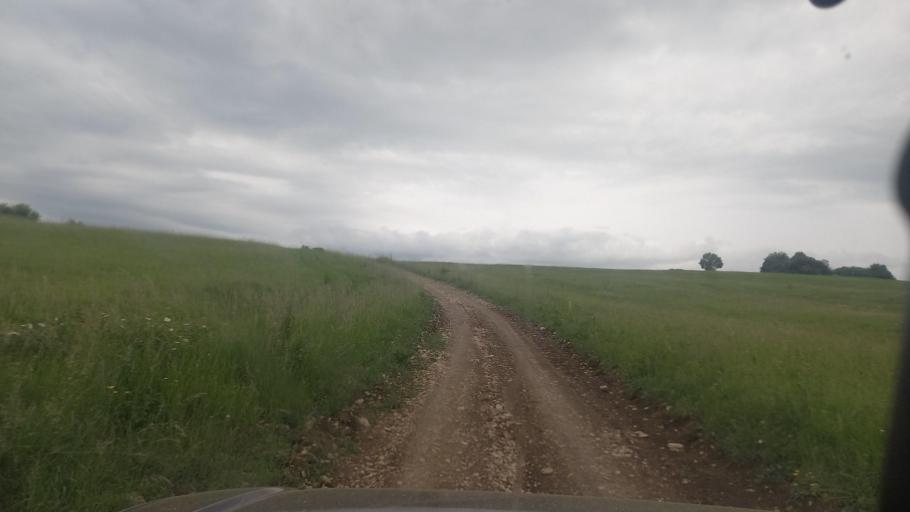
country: RU
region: Krasnodarskiy
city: Peredovaya
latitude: 44.0710
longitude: 41.3630
